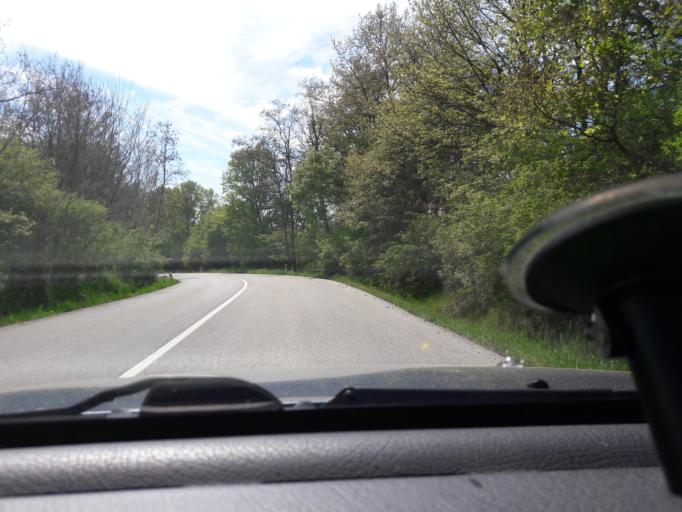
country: SK
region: Banskobystricky
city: Dudince
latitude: 48.2673
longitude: 18.7884
